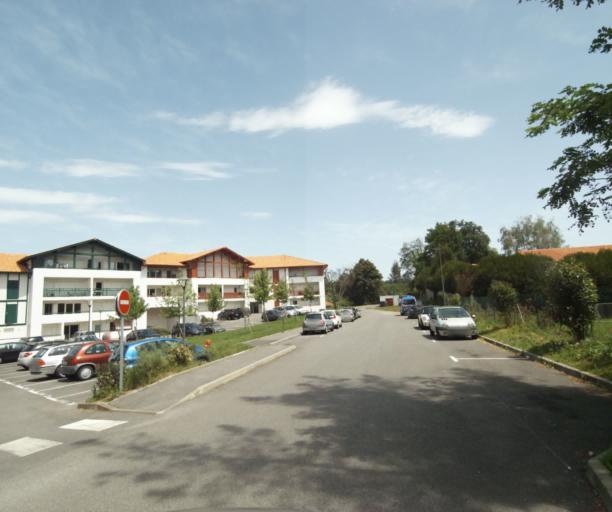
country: FR
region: Aquitaine
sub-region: Departement des Pyrenees-Atlantiques
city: Mouguerre
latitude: 43.4621
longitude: -1.4433
